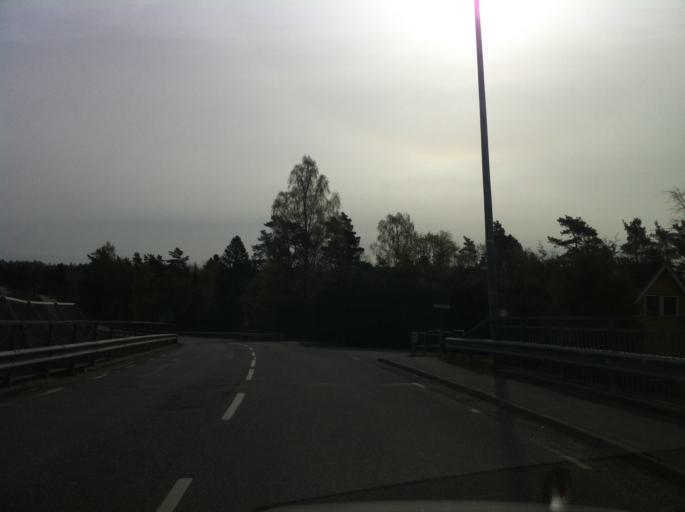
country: SE
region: Vaestra Goetaland
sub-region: Bollebygds Kommun
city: Bollebygd
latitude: 57.6684
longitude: 12.5756
